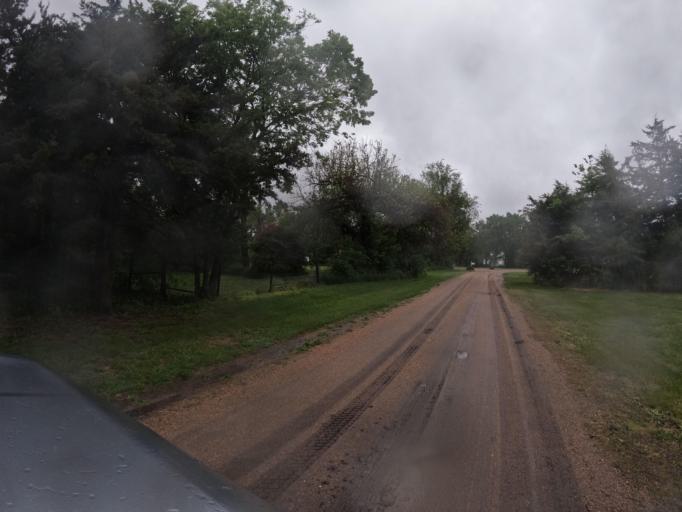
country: US
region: Nebraska
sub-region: Clay County
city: Harvard
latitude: 40.6212
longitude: -98.1027
